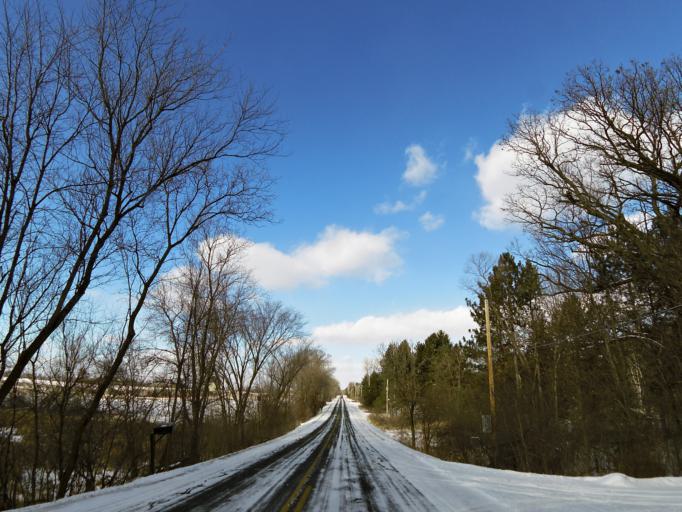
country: US
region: Minnesota
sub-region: Washington County
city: Lake Elmo
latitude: 44.9851
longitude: -92.8430
